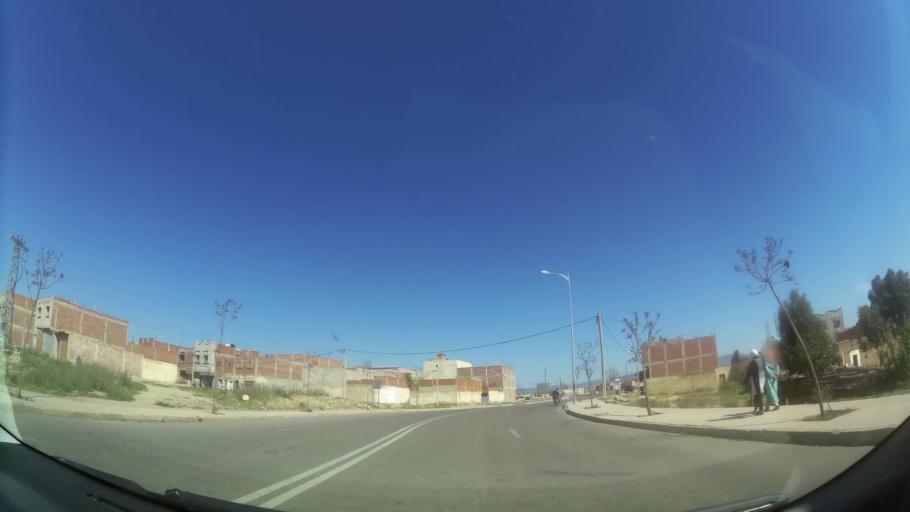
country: MA
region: Oriental
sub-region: Oujda-Angad
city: Oujda
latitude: 34.7214
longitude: -1.9056
